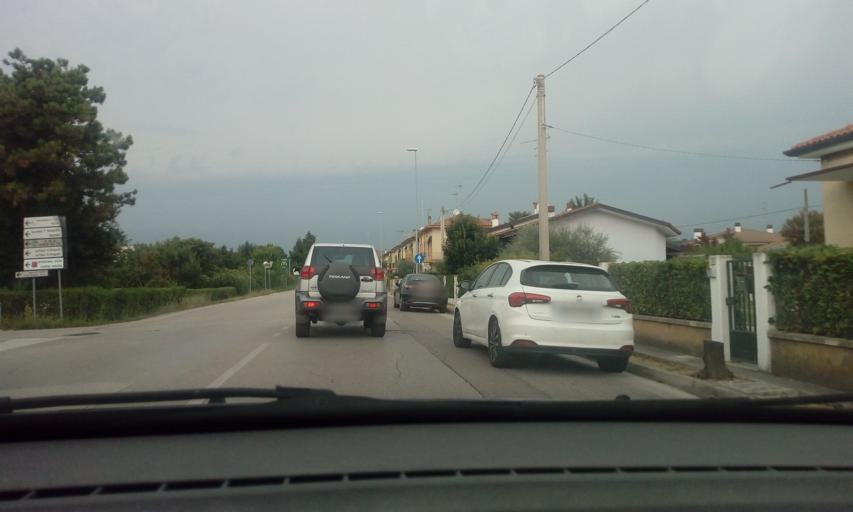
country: IT
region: Friuli Venezia Giulia
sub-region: Provincia di Gorizia
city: Ronchi dei Legionari
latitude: 45.8315
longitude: 13.4997
